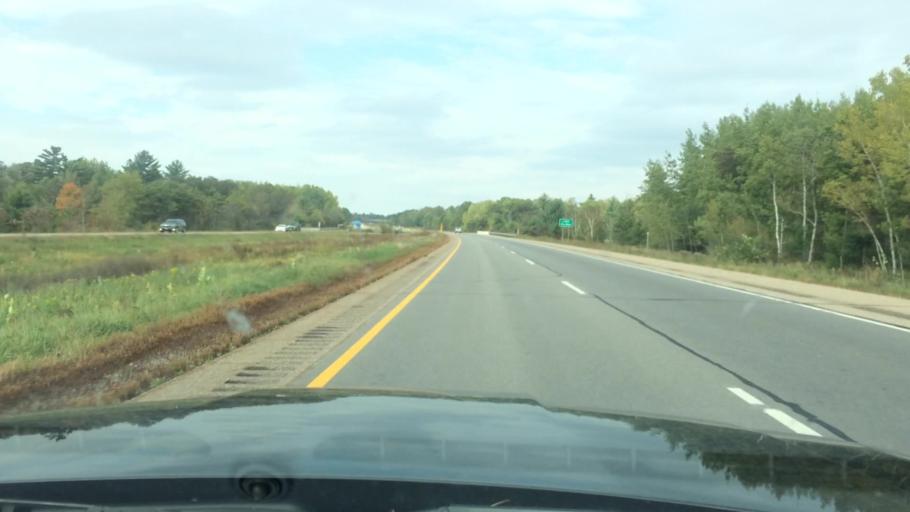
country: US
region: Wisconsin
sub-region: Marathon County
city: Mosinee
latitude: 44.7166
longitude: -89.6625
